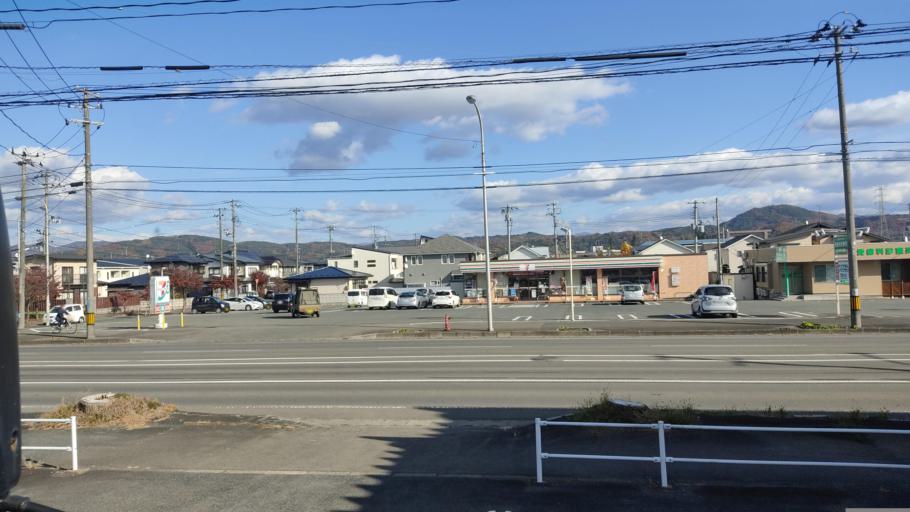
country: JP
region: Iwate
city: Morioka-shi
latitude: 39.6820
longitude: 141.1429
